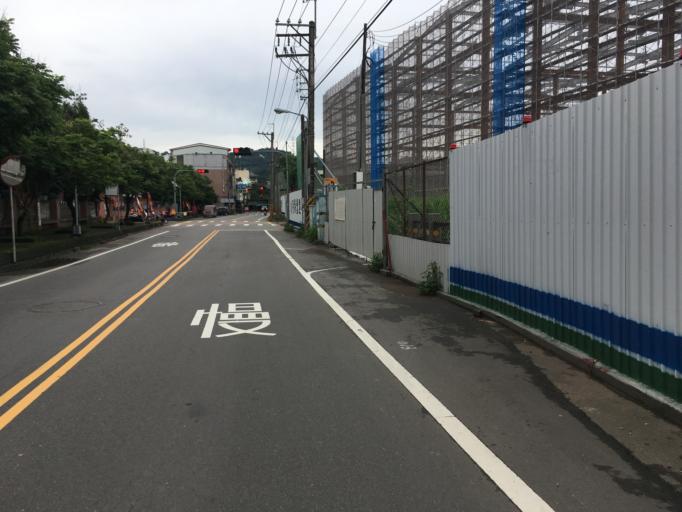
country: TW
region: Taiwan
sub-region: Taichung City
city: Taichung
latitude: 24.0804
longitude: 120.7187
